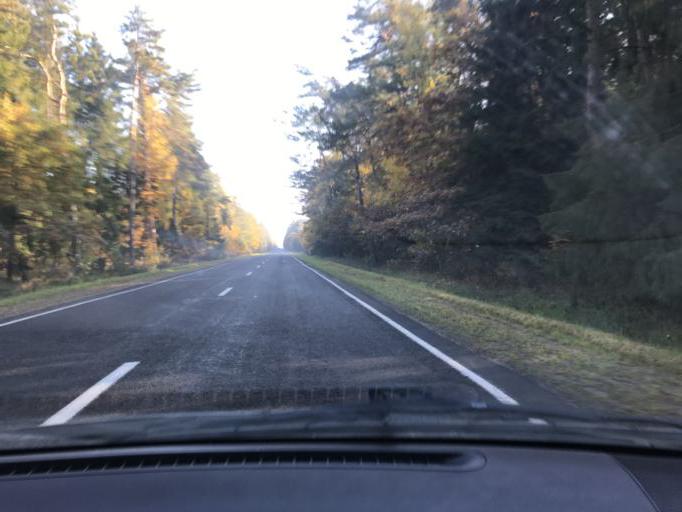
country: BY
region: Brest
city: Lyakhavichy
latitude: 52.9525
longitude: 26.2139
